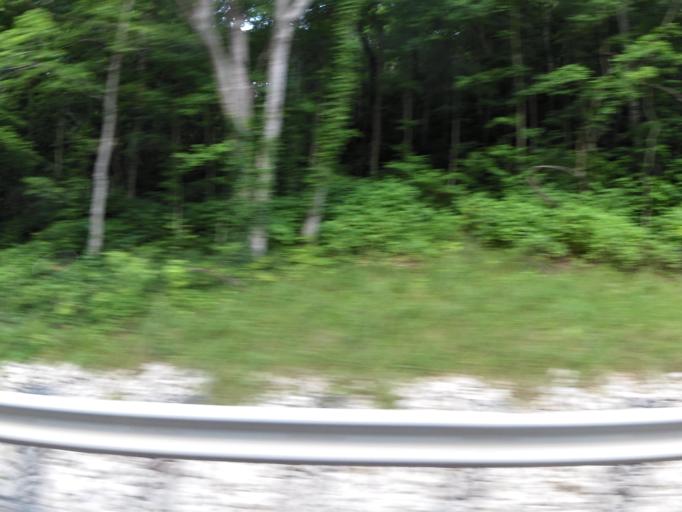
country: US
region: Missouri
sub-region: Saint Louis County
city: Eureka
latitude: 38.4673
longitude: -90.6253
